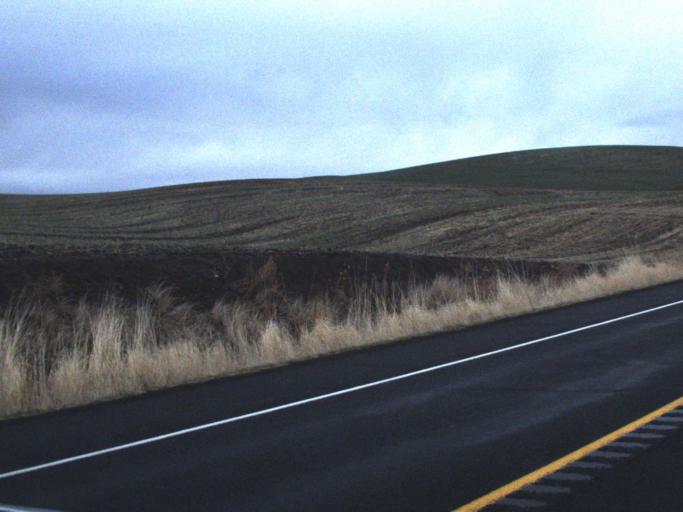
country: US
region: Washington
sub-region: Walla Walla County
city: Walla Walla East
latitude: 46.1289
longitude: -118.1887
